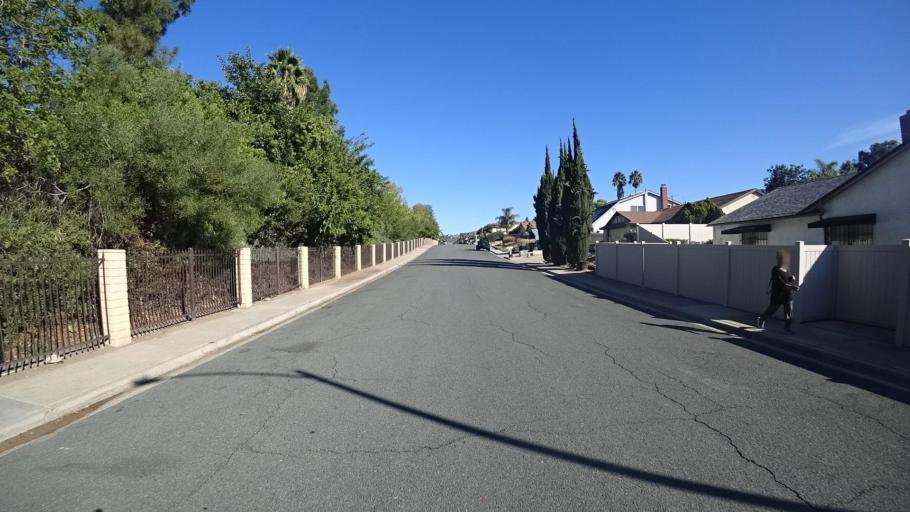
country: US
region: California
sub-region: San Diego County
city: La Presa
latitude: 32.7024
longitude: -116.9989
